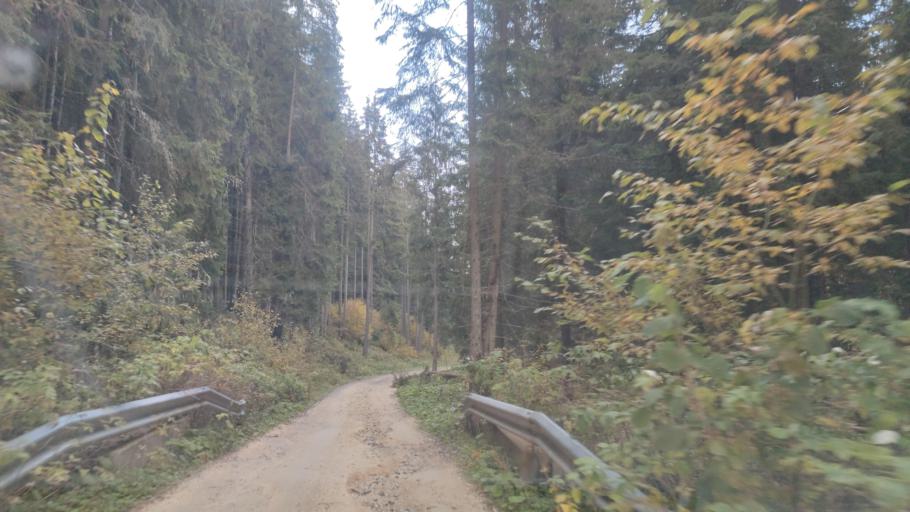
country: RO
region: Harghita
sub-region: Comuna Madaras
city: Madaras
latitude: 46.4779
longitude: 25.6515
